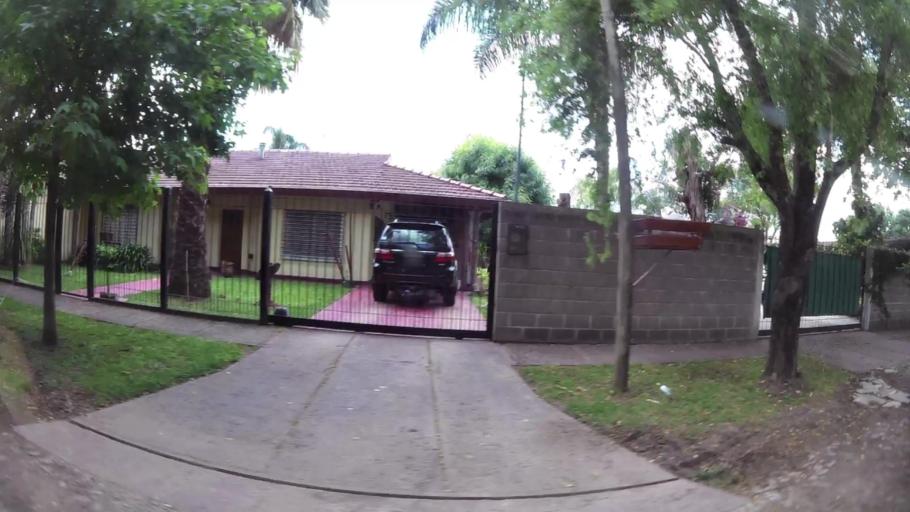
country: AR
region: Buenos Aires
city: Ituzaingo
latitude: -34.6379
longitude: -58.6736
